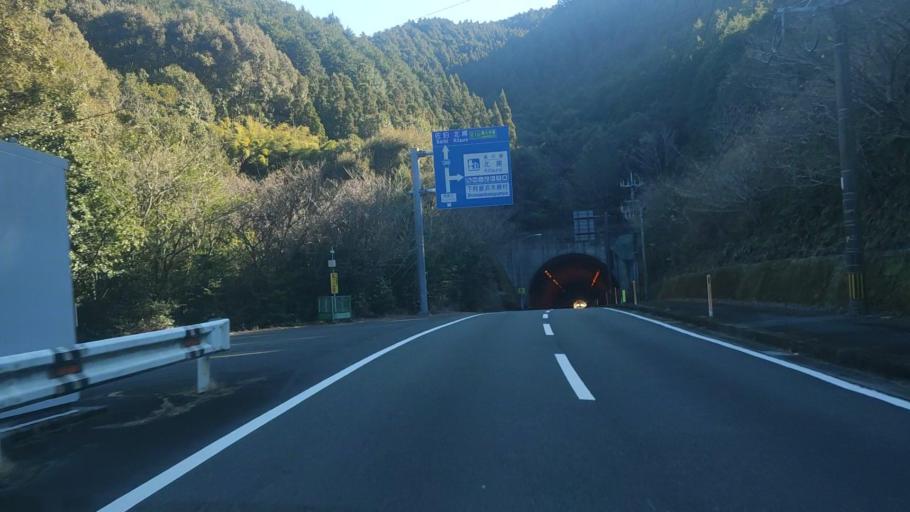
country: JP
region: Miyazaki
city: Nobeoka
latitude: 32.6867
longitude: 131.7912
